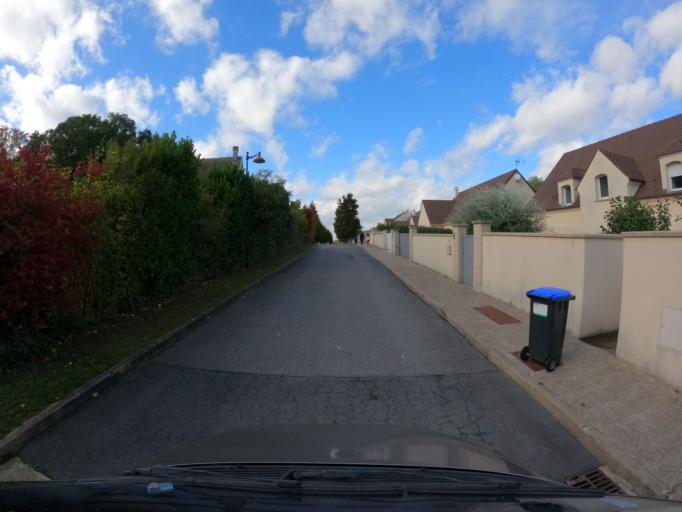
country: FR
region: Ile-de-France
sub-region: Departement de Seine-et-Marne
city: Esbly
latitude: 48.8927
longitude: 2.8167
